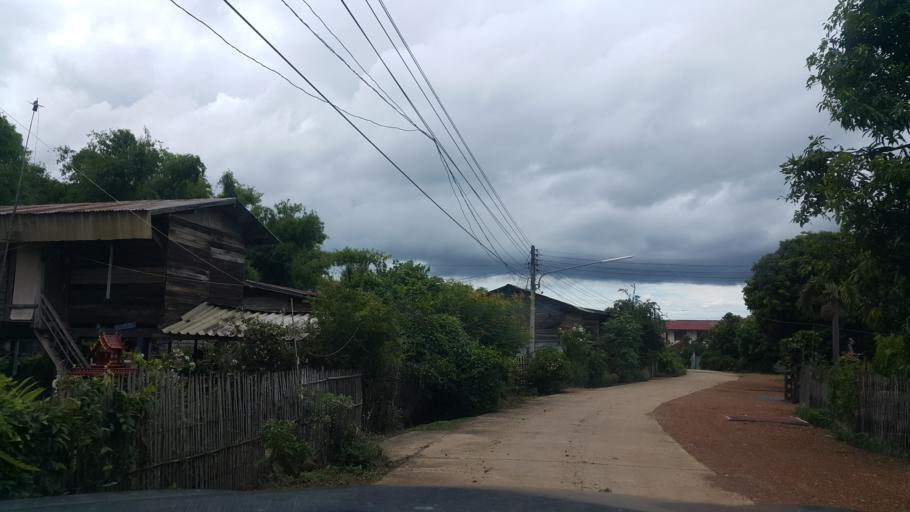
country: TH
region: Sukhothai
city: Thung Saliam
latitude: 17.3167
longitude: 99.5779
